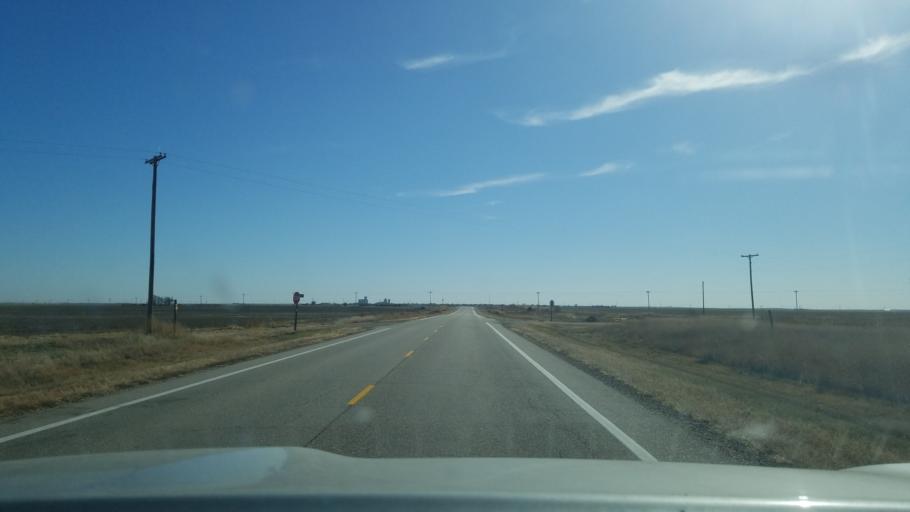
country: US
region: Kansas
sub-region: Kiowa County
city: Greensburg
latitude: 37.5739
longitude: -99.6674
